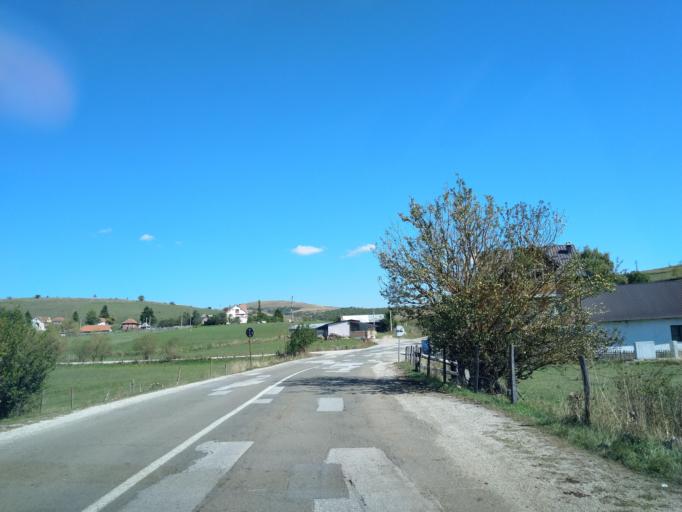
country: RS
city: Sokolovica
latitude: 43.2759
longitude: 20.1915
